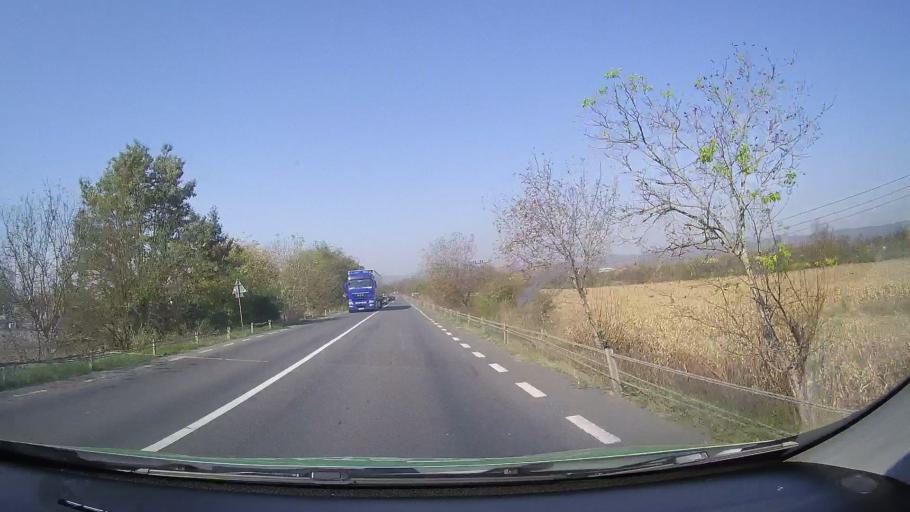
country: RO
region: Hunedoara
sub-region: Comuna Ilia
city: Ilia
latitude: 45.9258
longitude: 22.6651
